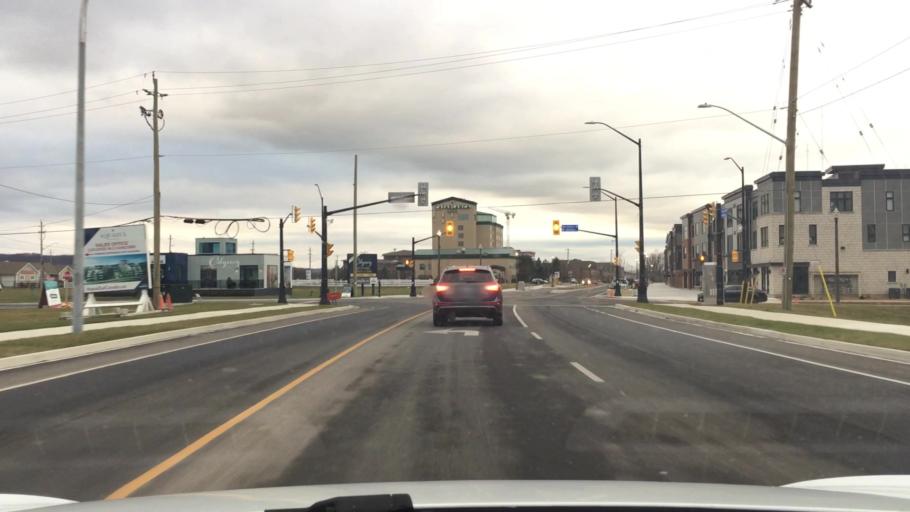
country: CA
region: Ontario
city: Oakville
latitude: 43.2099
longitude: -79.5977
